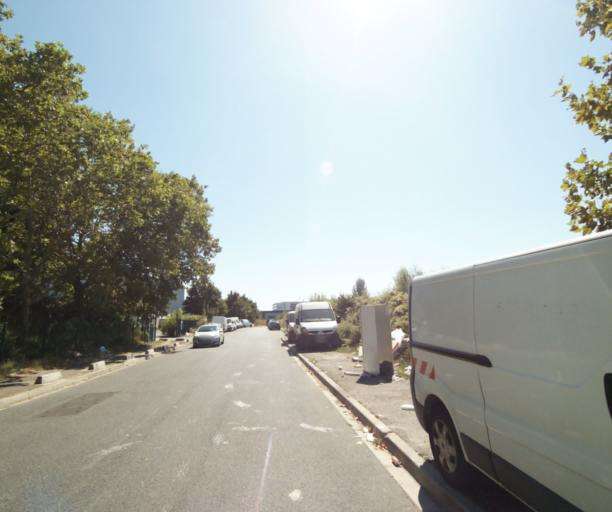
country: FR
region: Ile-de-France
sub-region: Departement des Hauts-de-Seine
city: Villeneuve-la-Garenne
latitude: 48.9440
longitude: 2.3102
